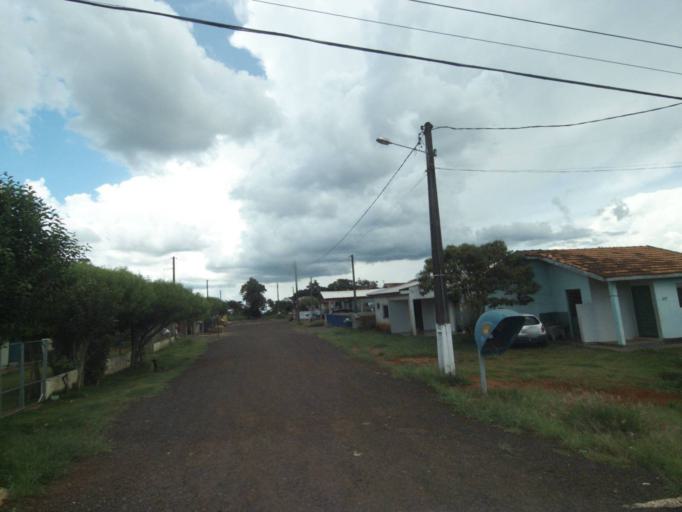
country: BR
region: Parana
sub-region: Guaraniacu
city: Guaraniacu
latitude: -25.1046
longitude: -52.8581
